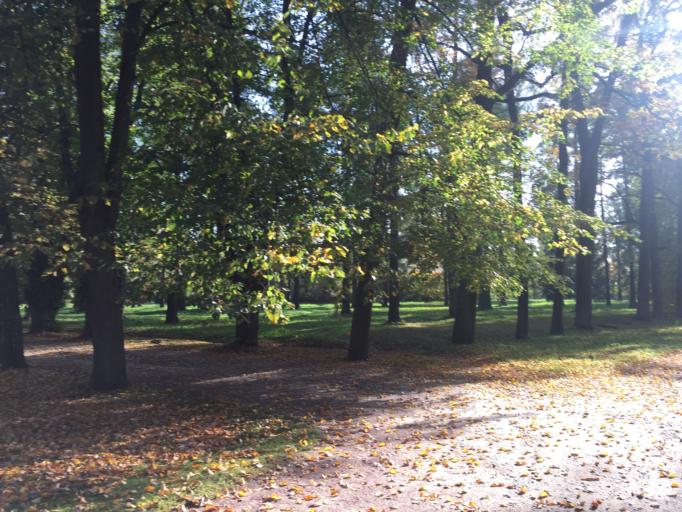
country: RU
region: St.-Petersburg
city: Pushkin
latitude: 59.7190
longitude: 30.3858
